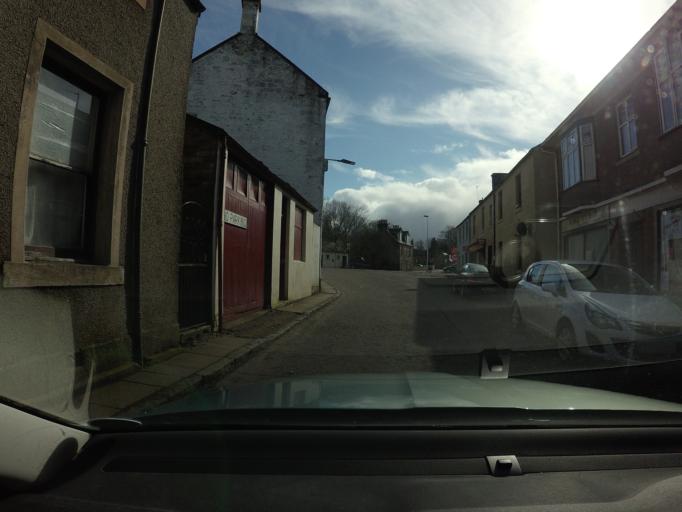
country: GB
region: Scotland
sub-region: South Lanarkshire
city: Douglas
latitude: 55.5560
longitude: -3.8483
